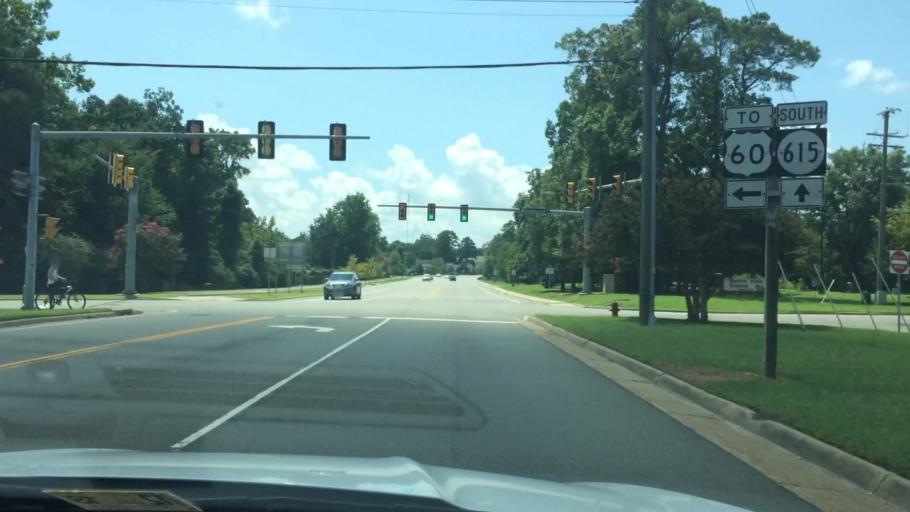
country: US
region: Virginia
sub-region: James City County
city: Williamsburg
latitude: 37.2897
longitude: -76.7339
